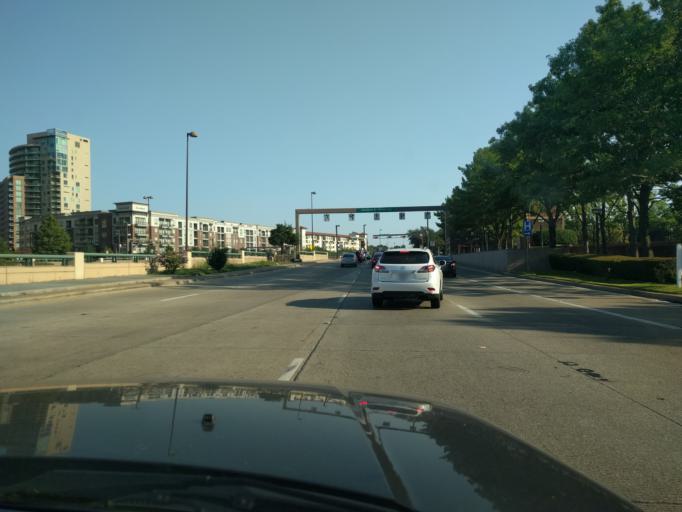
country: US
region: Texas
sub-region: Dallas County
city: Dallas
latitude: 32.8061
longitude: -96.7929
